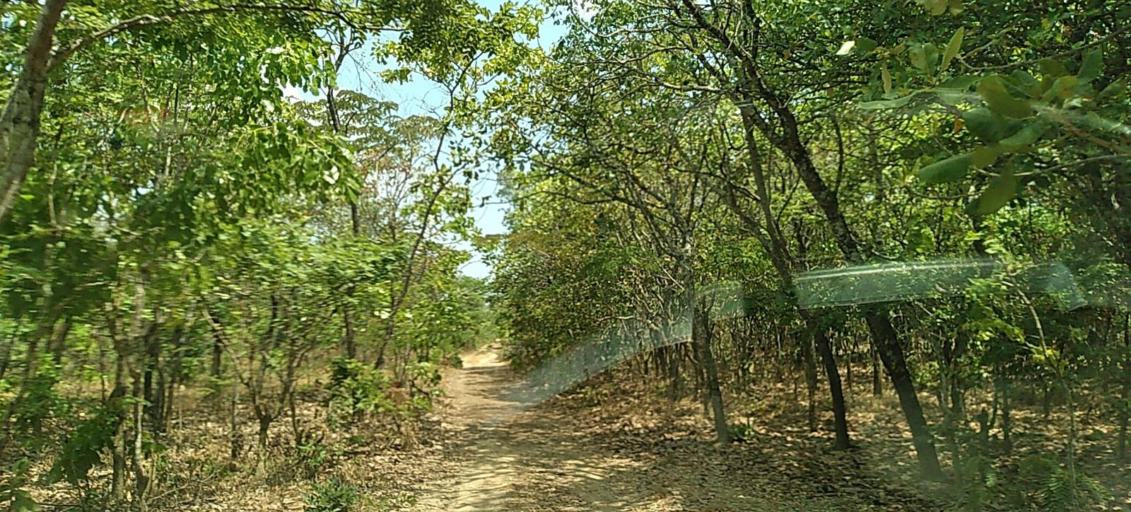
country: CD
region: Katanga
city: Kipushi
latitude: -11.9765
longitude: 27.4143
